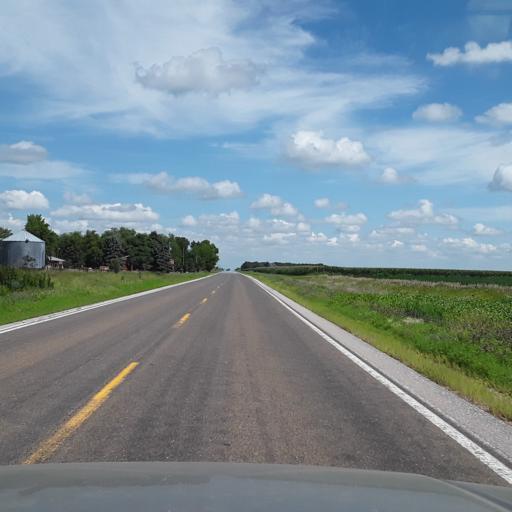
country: US
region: Nebraska
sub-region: Polk County
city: Osceola
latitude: 41.0376
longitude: -97.4063
